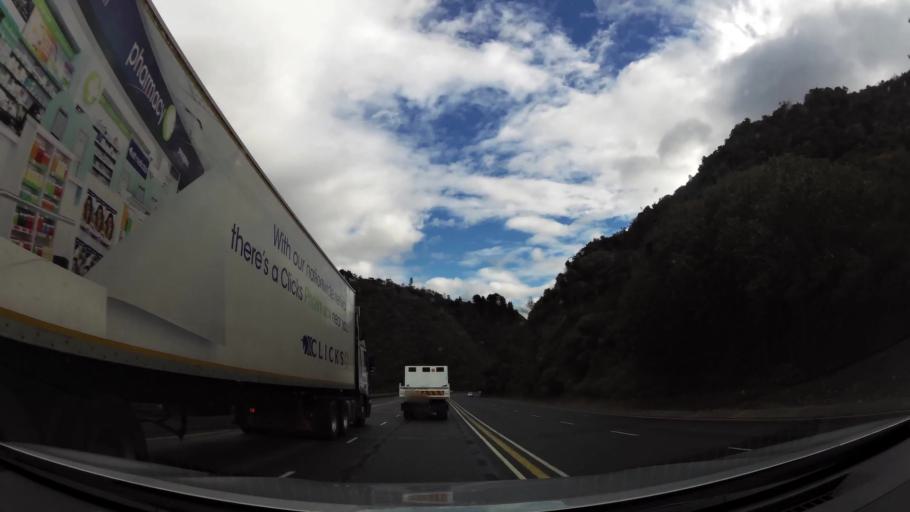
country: ZA
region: Western Cape
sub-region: Eden District Municipality
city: George
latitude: -33.9951
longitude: 22.5554
